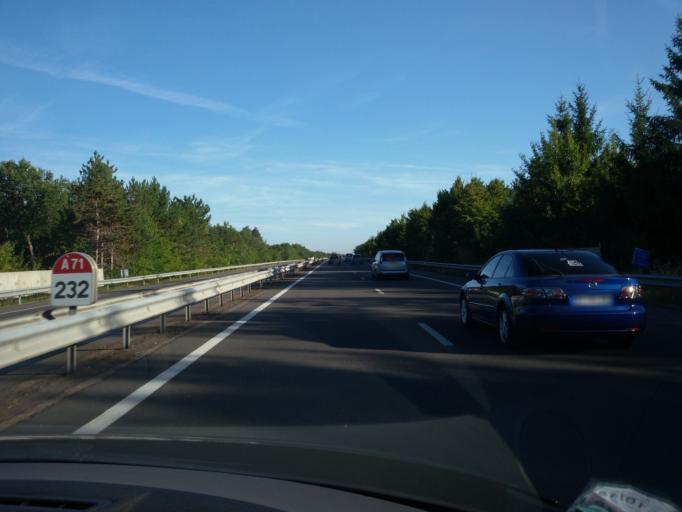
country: FR
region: Centre
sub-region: Departement du Cher
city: Levet
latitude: 46.8733
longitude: 2.4246
